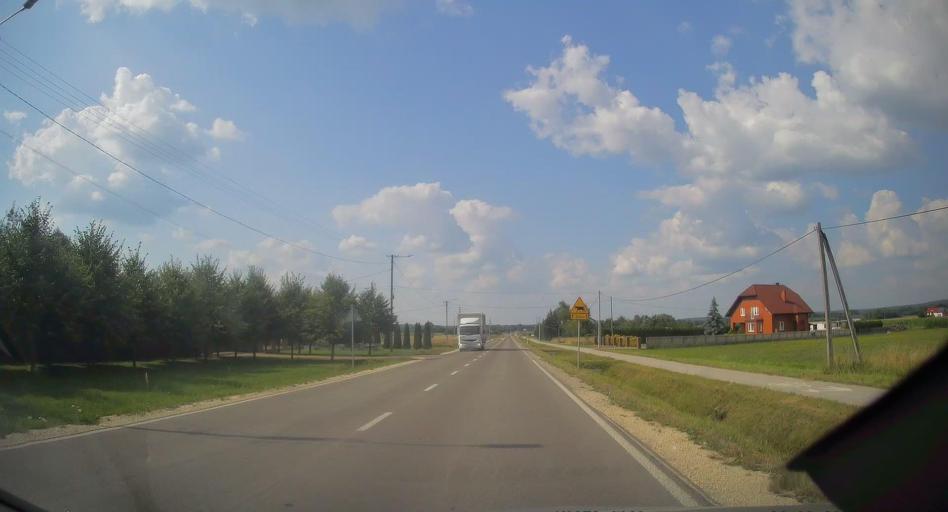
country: PL
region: Swietokrzyskie
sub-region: Powiat kielecki
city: Lopuszno
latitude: 50.9537
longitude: 20.2512
